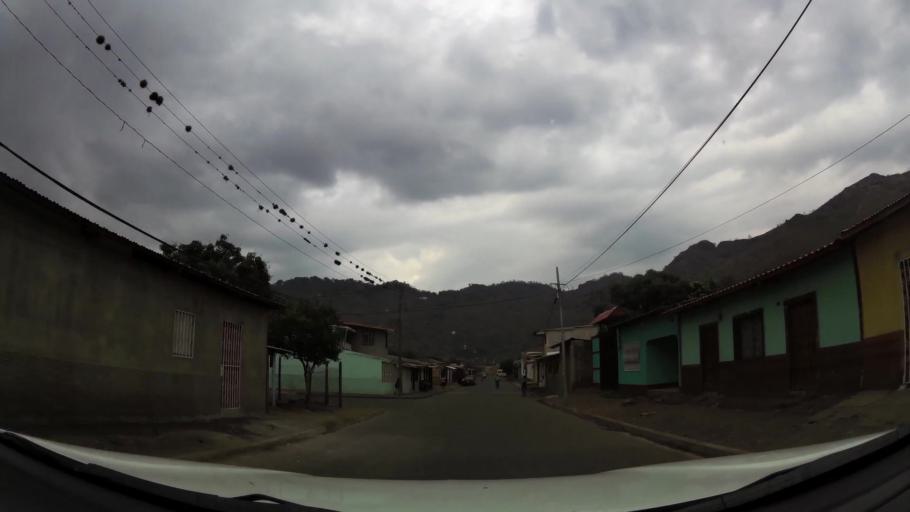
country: NI
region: Jinotega
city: Jinotega
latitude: 13.0958
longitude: -85.9992
